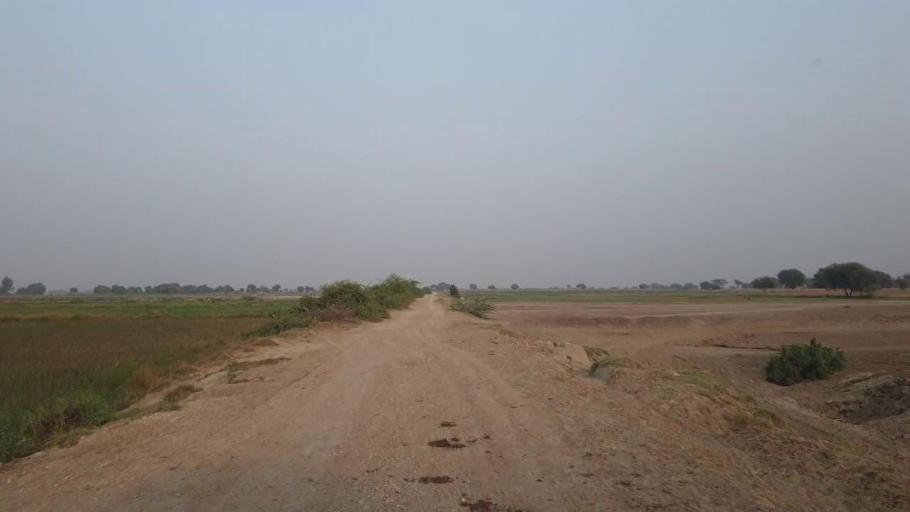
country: PK
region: Sindh
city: Mirpur Batoro
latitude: 24.6605
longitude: 68.3800
